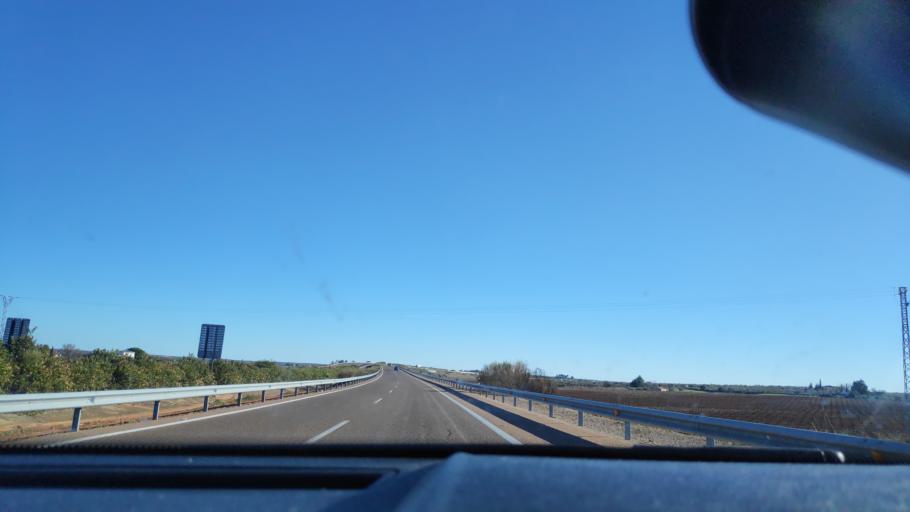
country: ES
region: Extremadura
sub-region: Provincia de Badajoz
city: Villafranca de los Barros
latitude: 38.5340
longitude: -6.3579
